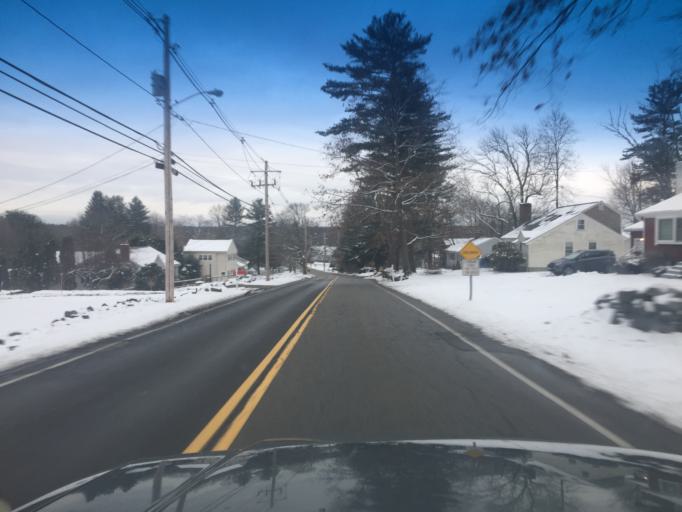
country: US
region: Massachusetts
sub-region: Middlesex County
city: Holliston
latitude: 42.1892
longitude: -71.4161
